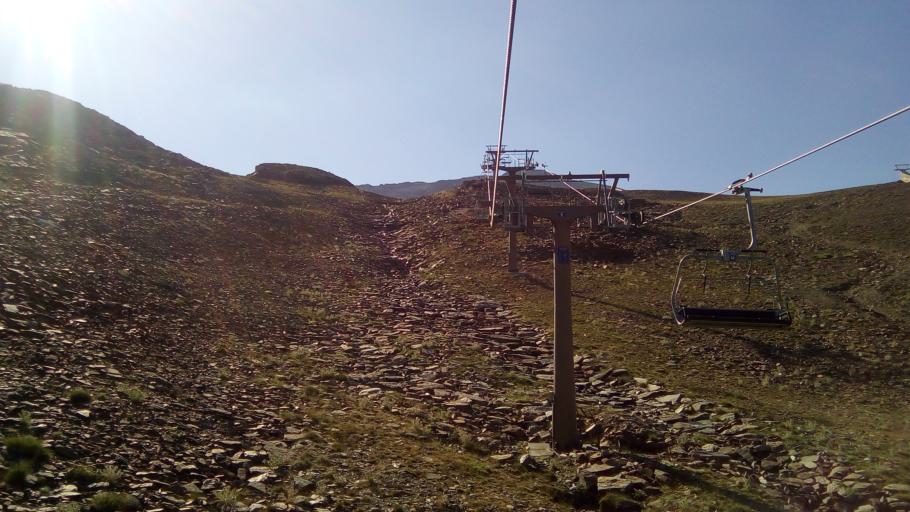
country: ES
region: Andalusia
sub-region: Provincia de Granada
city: Guejar-Sierra
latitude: 37.0686
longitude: -3.3835
